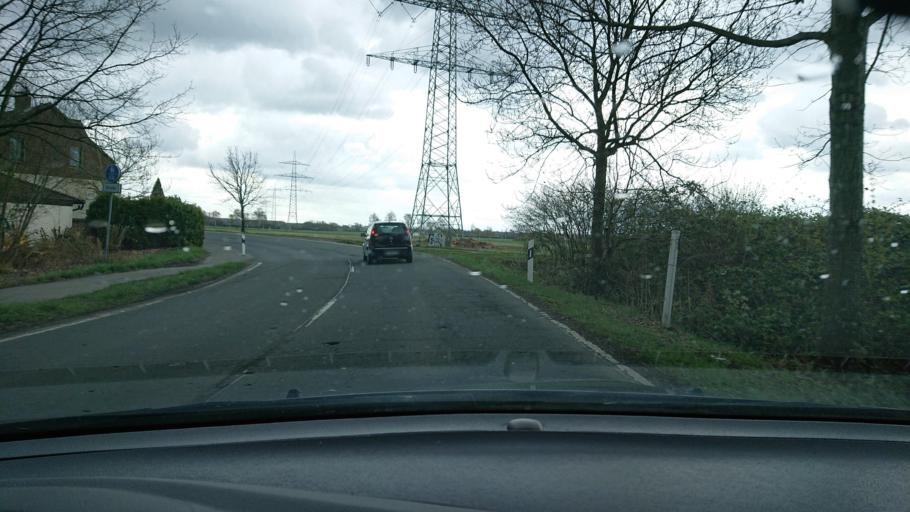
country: DE
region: North Rhine-Westphalia
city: Lanstrop
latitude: 51.5382
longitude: 7.5811
